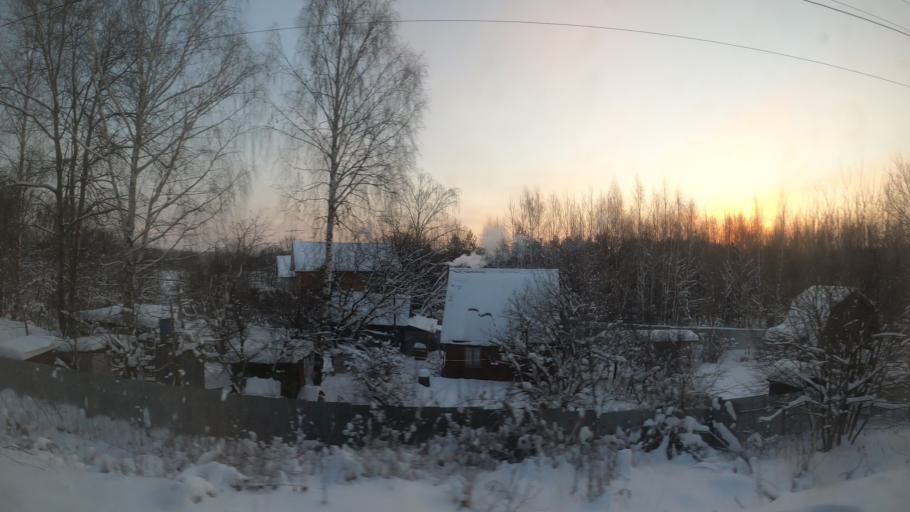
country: RU
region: Moskovskaya
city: Yermolino
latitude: 56.1453
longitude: 37.5069
